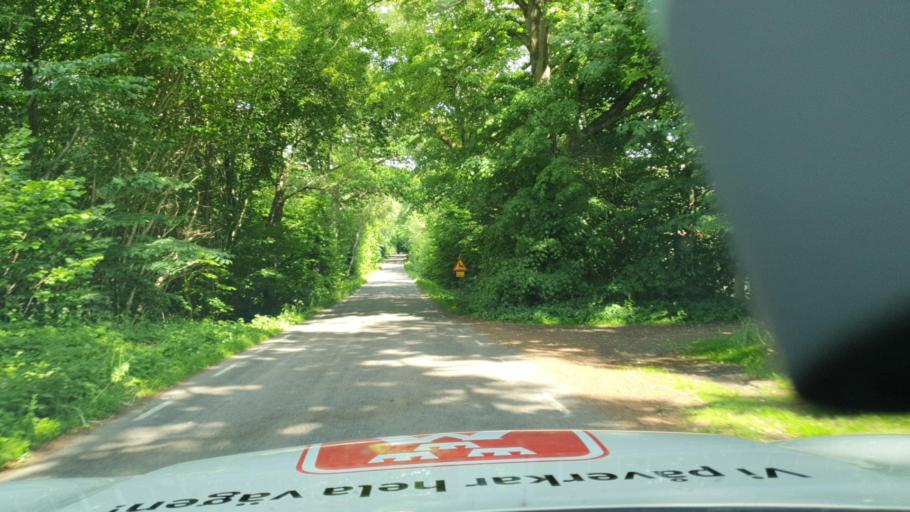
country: SE
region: Skane
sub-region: Svedala Kommun
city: Svedala
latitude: 55.5343
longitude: 13.2367
